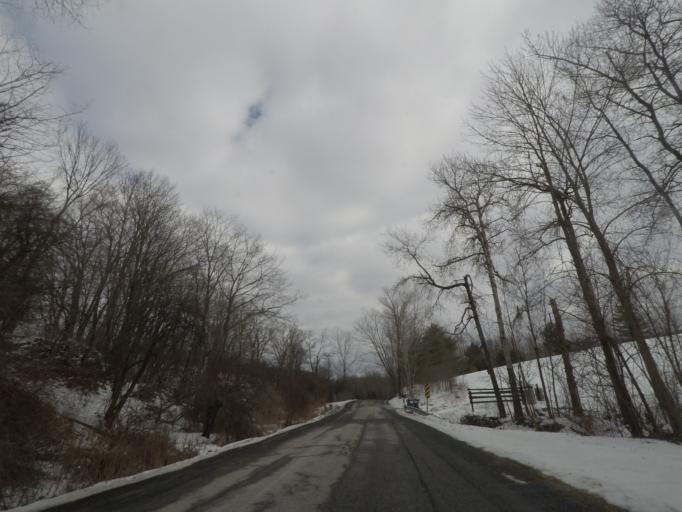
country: US
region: New York
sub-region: Rensselaer County
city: Hoosick Falls
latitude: 42.8658
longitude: -73.3811
